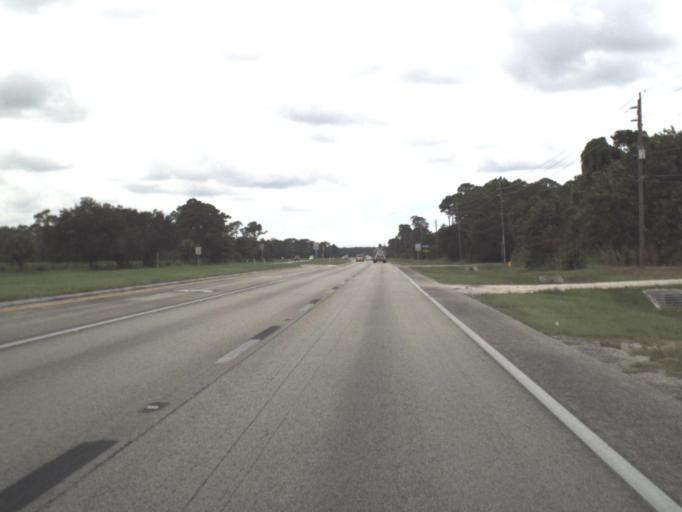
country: US
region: Florida
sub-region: Lee County
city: Alva
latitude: 26.7089
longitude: -81.6138
